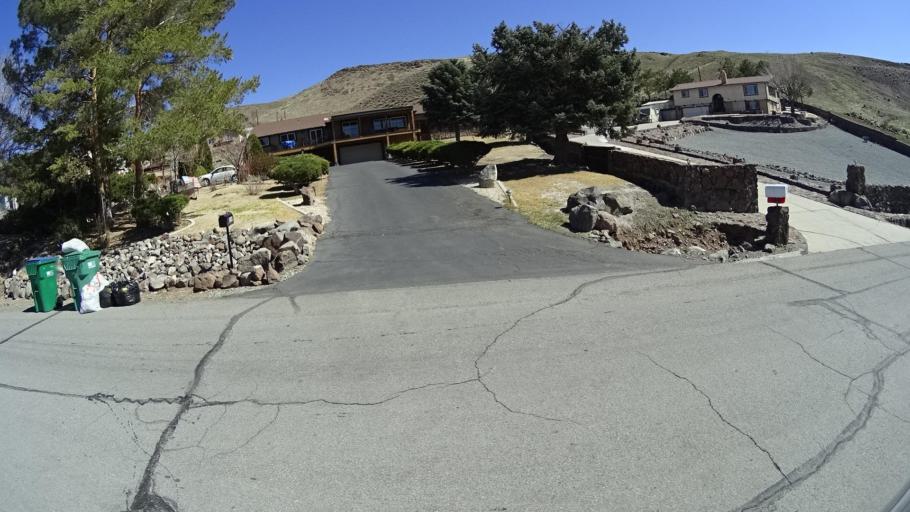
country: US
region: Nevada
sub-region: Washoe County
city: Sparks
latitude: 39.5437
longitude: -119.6954
